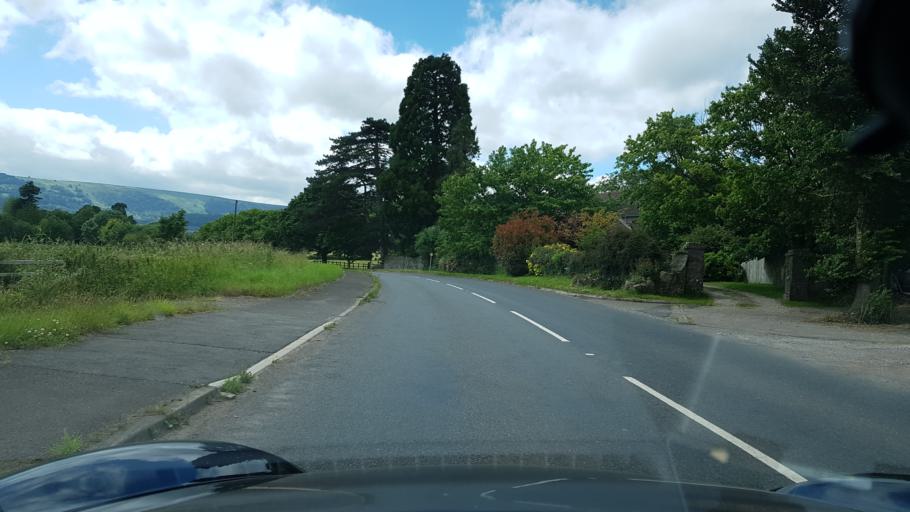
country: GB
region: Wales
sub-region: Monmouthshire
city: Abergavenny
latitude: 51.7866
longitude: -2.9673
